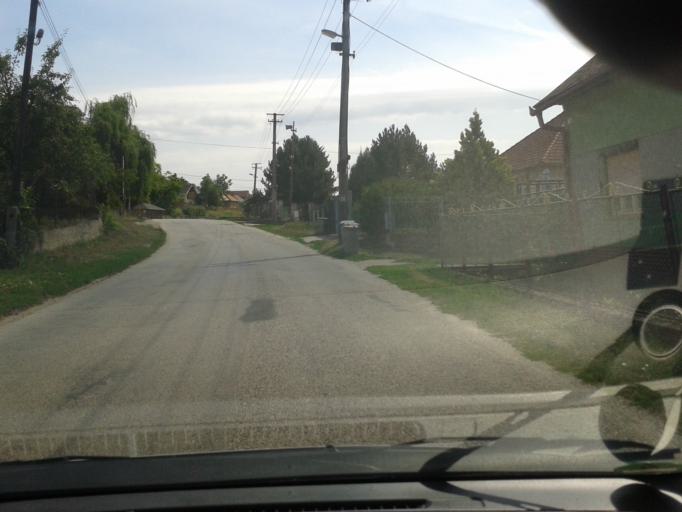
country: HU
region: Pest
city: Szob
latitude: 47.8281
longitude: 18.8142
